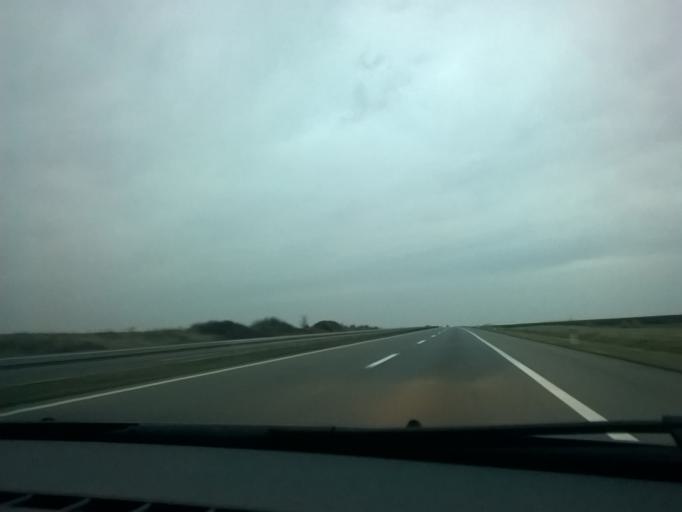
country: RS
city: Beska
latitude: 45.1150
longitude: 20.0997
